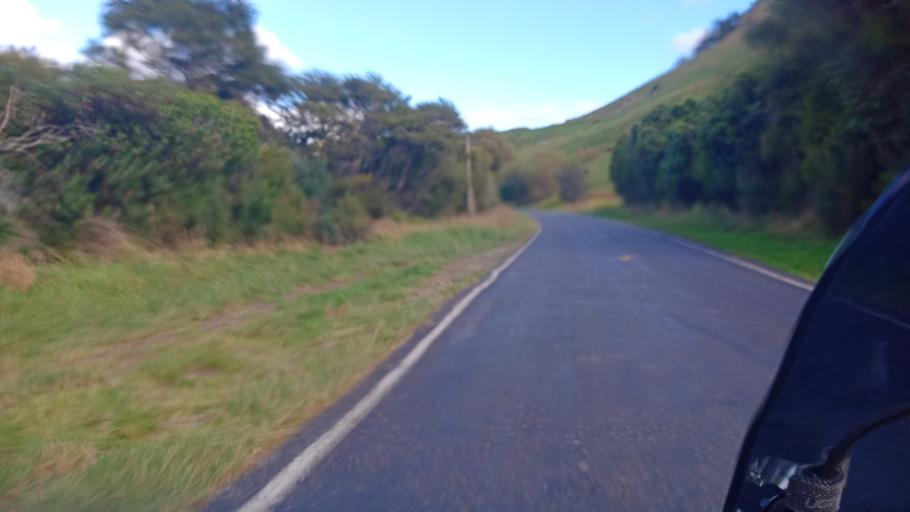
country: NZ
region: Gisborne
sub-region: Gisborne District
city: Gisborne
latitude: -38.5375
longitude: 177.5758
